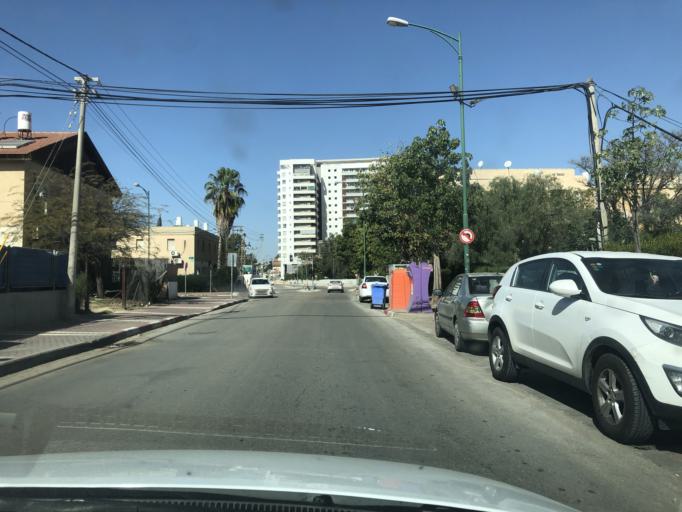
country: IL
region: Southern District
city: Beersheba
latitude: 31.2572
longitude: 34.7952
